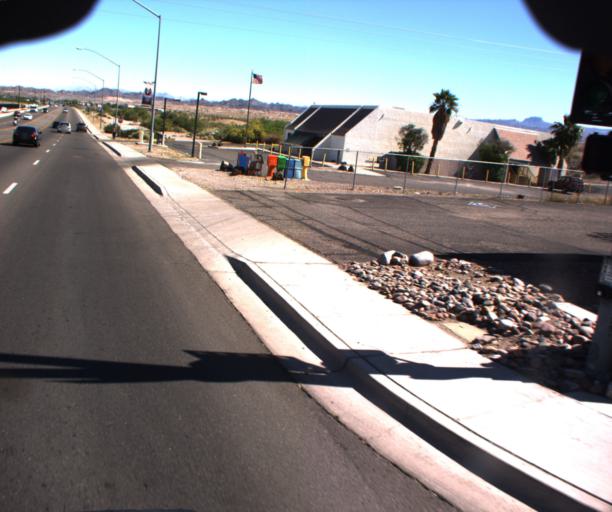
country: US
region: Arizona
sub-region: Mohave County
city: Bullhead City
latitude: 35.1532
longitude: -114.5674
